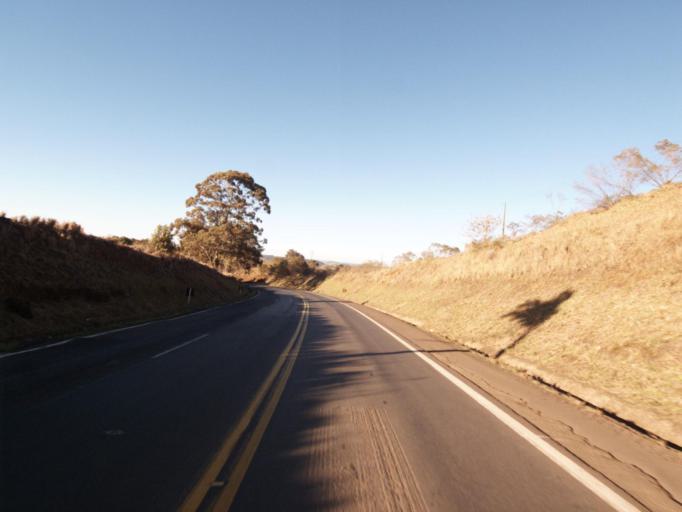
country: AR
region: Misiones
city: Bernardo de Irigoyen
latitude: -26.3211
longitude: -53.5505
